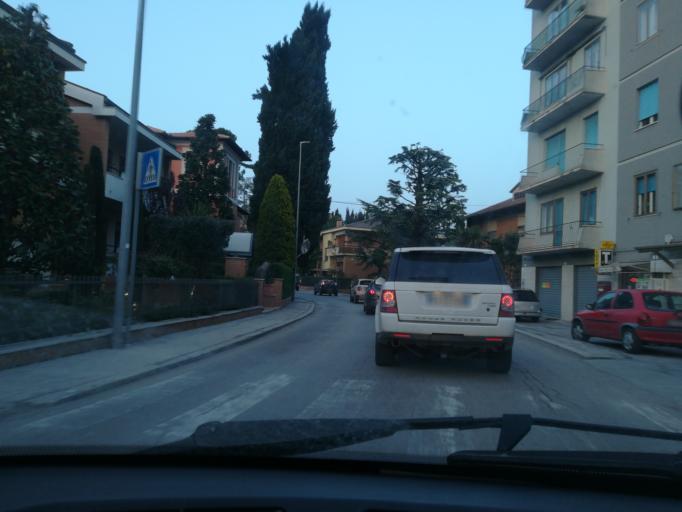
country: IT
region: The Marches
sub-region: Provincia di Macerata
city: Macerata
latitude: 43.2898
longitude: 13.4556
